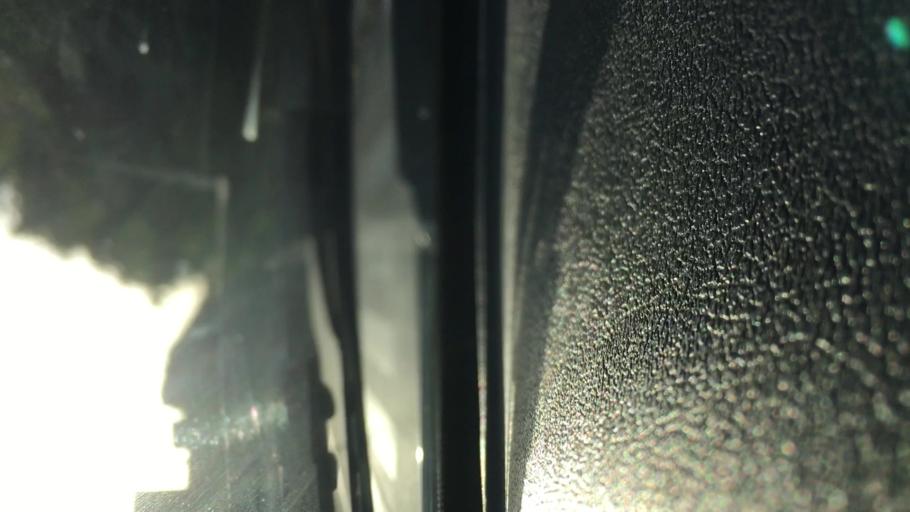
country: IT
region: Latium
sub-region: Citta metropolitana di Roma Capitale
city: Rome
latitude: 41.8323
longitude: 12.5077
